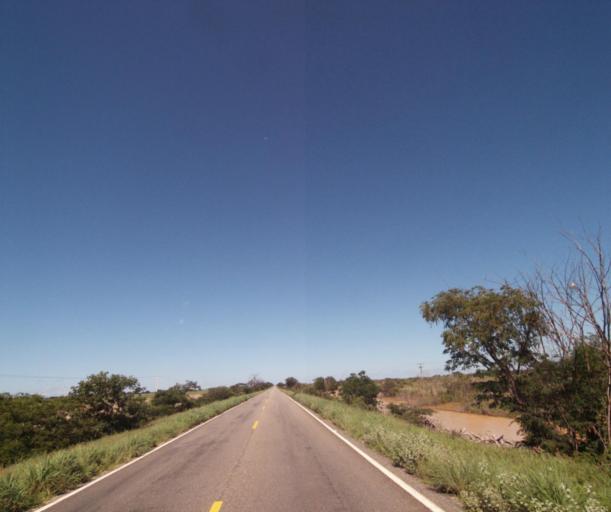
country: BR
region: Bahia
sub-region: Palmas De Monte Alto
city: Palmas de Monte Alto
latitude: -14.2653
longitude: -43.3559
